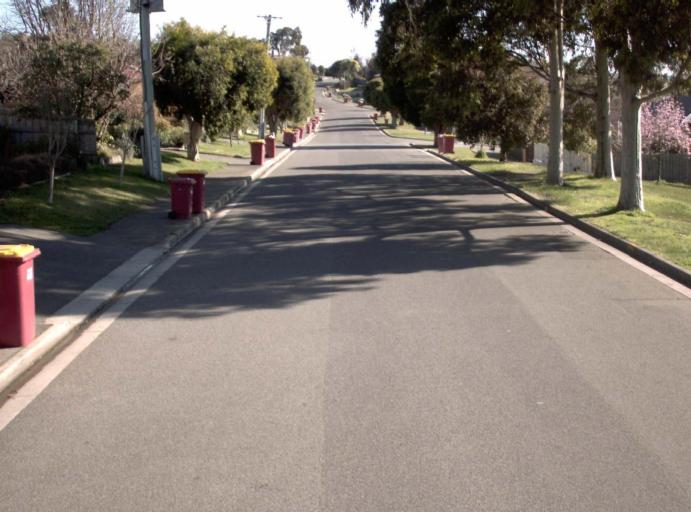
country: AU
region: Tasmania
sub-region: Launceston
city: East Launceston
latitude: -41.4508
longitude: 147.1573
